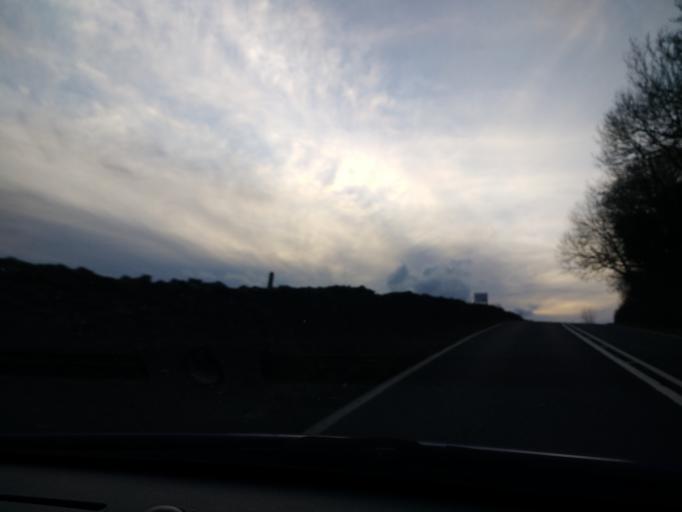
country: GB
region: England
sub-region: North Yorkshire
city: Settle
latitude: 54.1065
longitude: -2.3693
